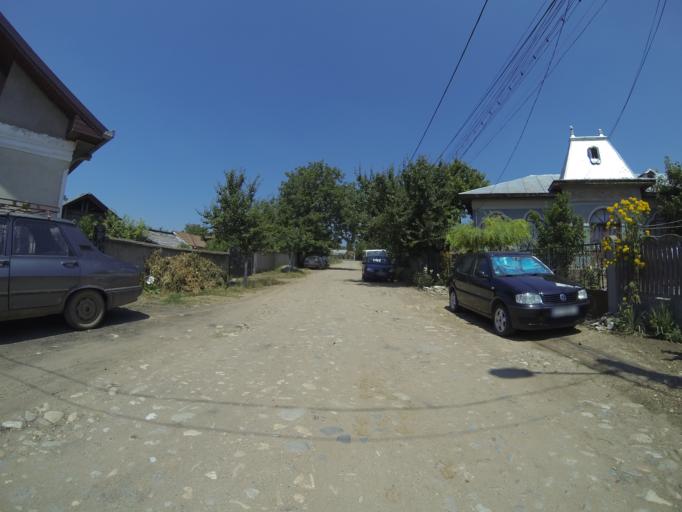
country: RO
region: Dolj
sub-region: Comuna Segarcea
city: Segarcea
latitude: 44.0928
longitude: 23.7529
